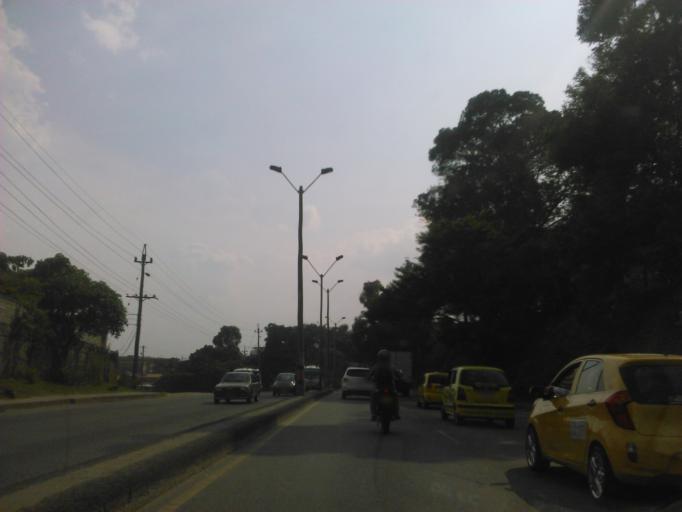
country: CO
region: Antioquia
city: Bello
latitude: 6.3000
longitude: -75.5651
